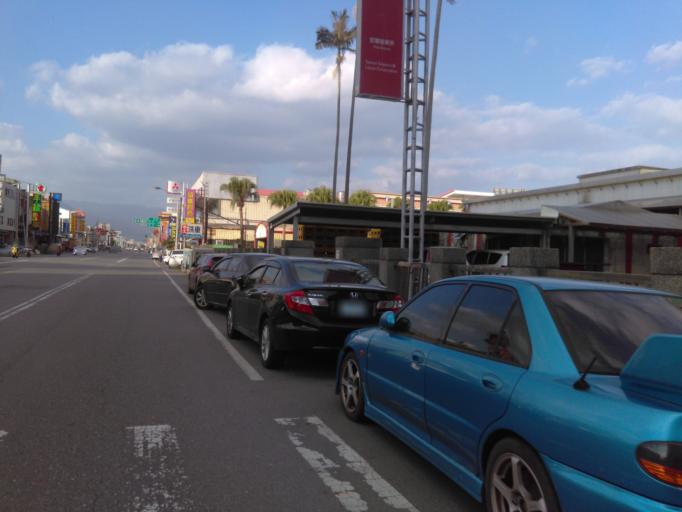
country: TW
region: Taiwan
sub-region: Yilan
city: Yilan
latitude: 24.7700
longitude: 121.7569
